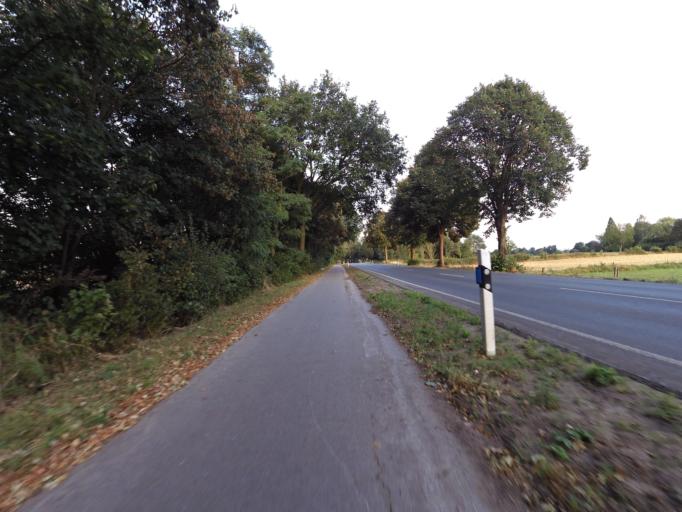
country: DE
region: North Rhine-Westphalia
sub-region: Regierungsbezirk Dusseldorf
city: Emmerich
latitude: 51.8617
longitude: 6.1816
